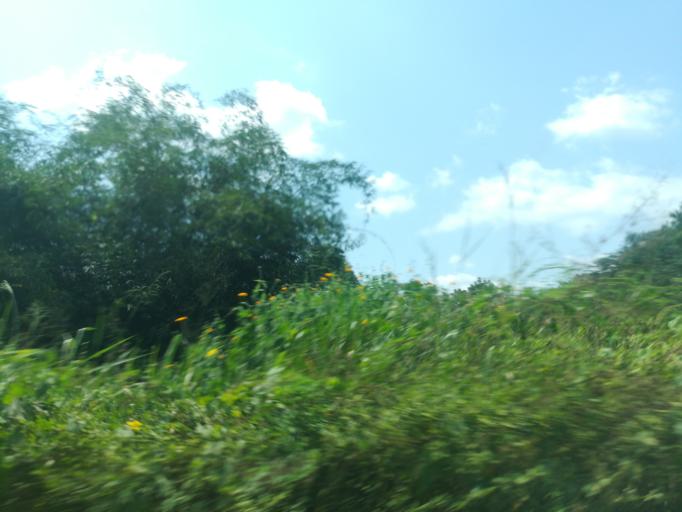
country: NG
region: Oyo
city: Moniya
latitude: 7.5571
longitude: 3.9098
